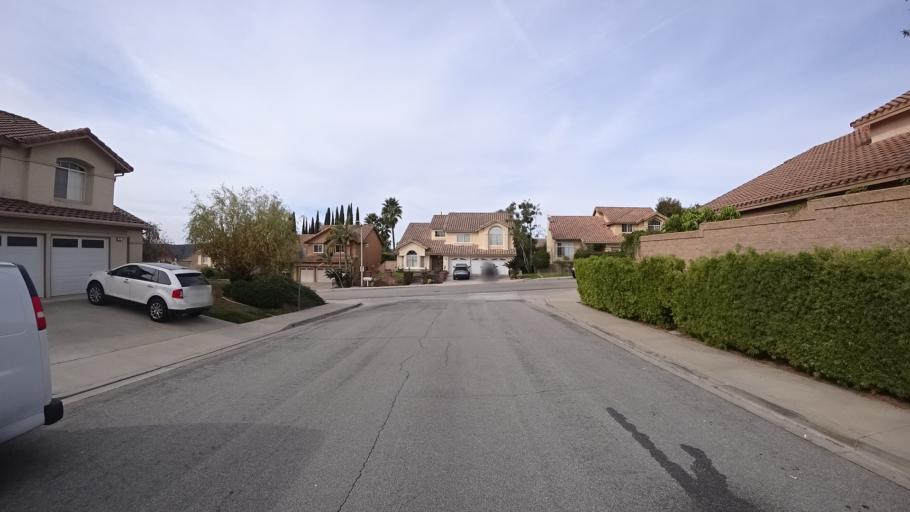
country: US
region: California
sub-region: Orange County
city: Laguna Woods
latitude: 33.5918
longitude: -117.7404
